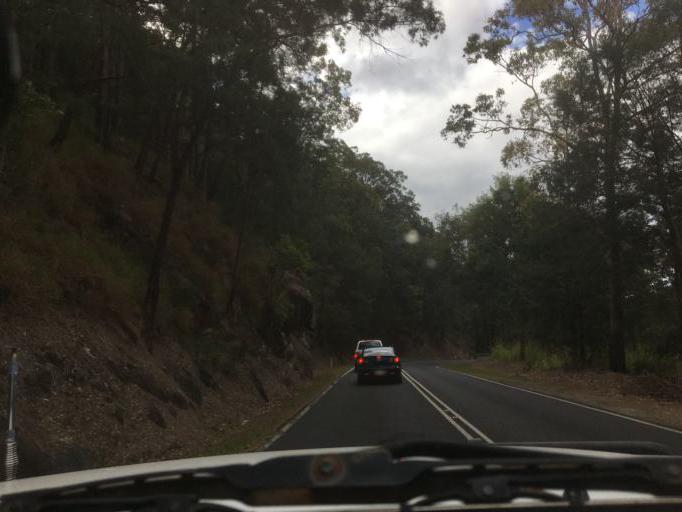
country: AU
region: Queensland
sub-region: Tablelands
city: Tolga
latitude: -17.2161
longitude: 145.6988
